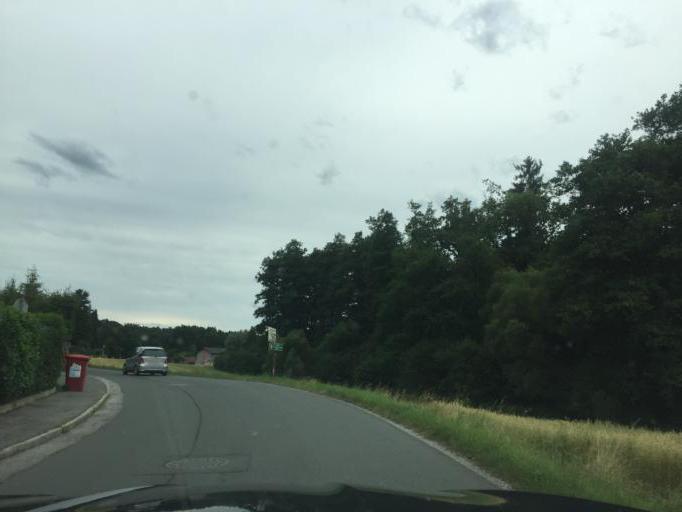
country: AT
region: Styria
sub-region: Politischer Bezirk Graz-Umgebung
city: Hart bei Graz
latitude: 47.0496
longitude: 15.5112
